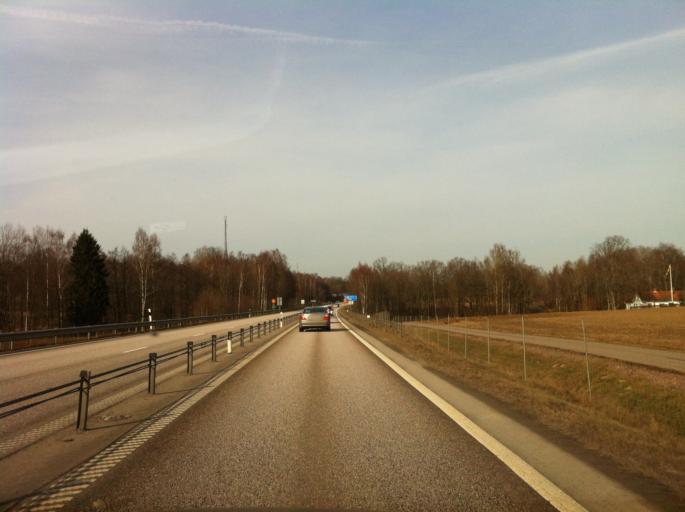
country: SE
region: Vaestra Goetaland
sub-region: Skovde Kommun
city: Stopen
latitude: 58.4469
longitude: 13.8515
